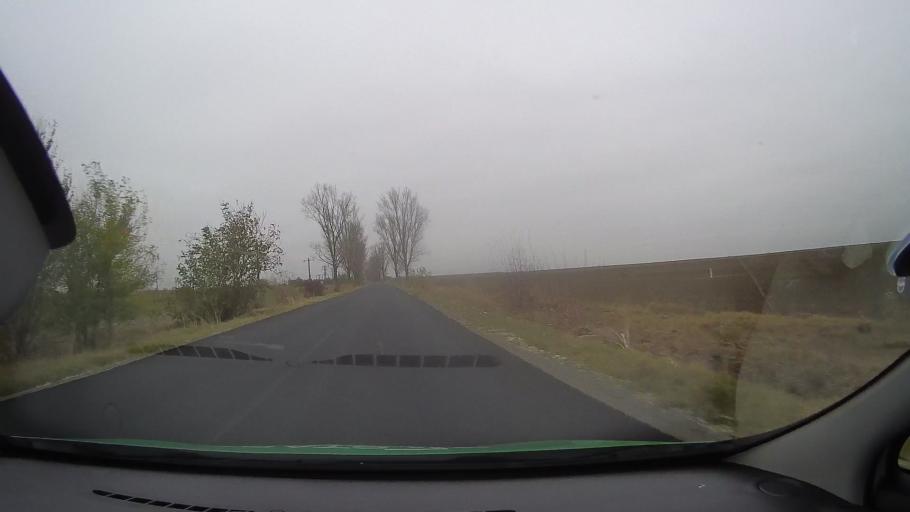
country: RO
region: Ialomita
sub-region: Comuna Valea Ciorii
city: Valea Ciorii
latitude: 44.7469
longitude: 27.5718
